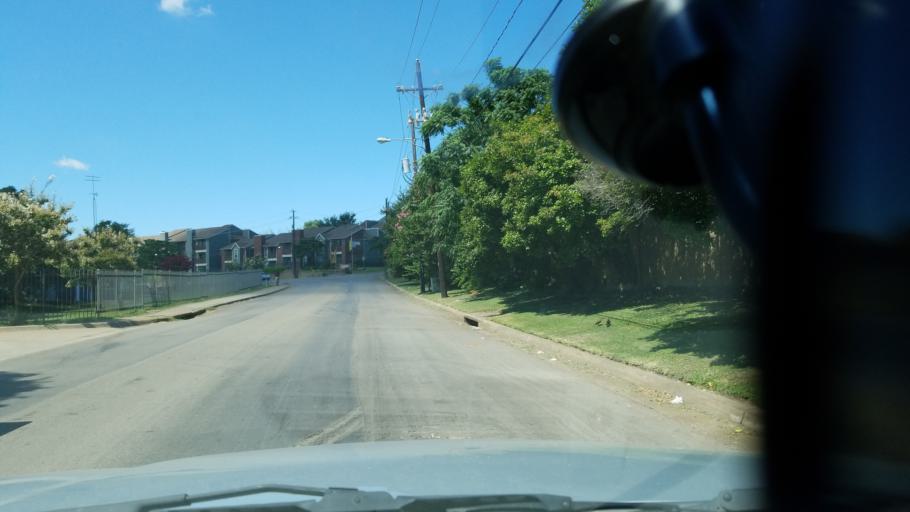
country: US
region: Texas
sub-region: Dallas County
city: Duncanville
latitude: 32.6606
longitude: -96.8689
